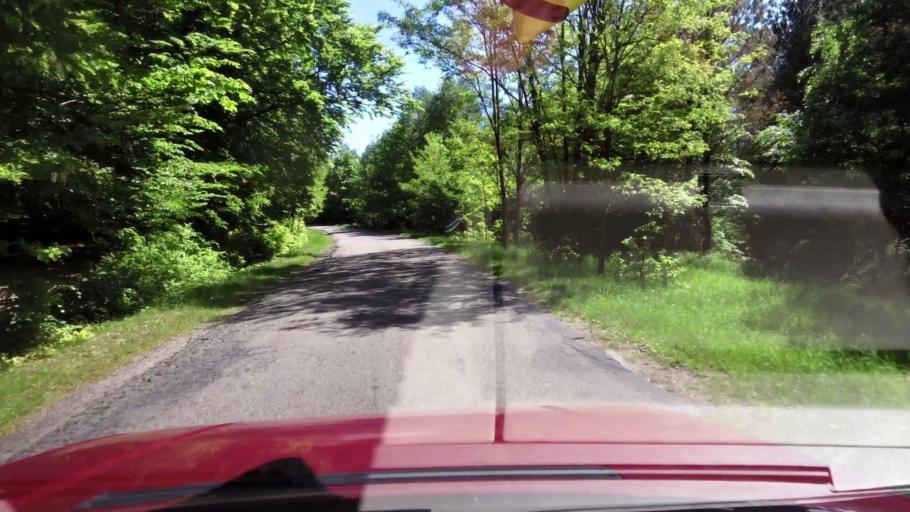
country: PL
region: West Pomeranian Voivodeship
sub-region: Powiat koszalinski
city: Bobolice
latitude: 54.0701
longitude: 16.5056
